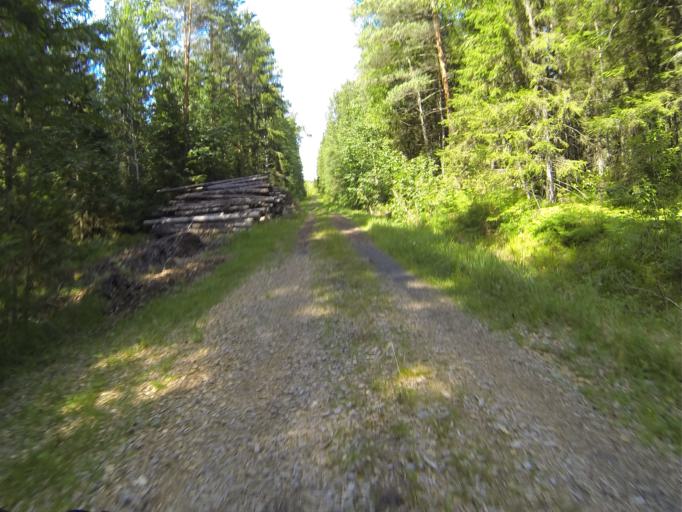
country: FI
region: Varsinais-Suomi
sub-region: Salo
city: Pernioe
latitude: 60.2786
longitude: 23.0594
